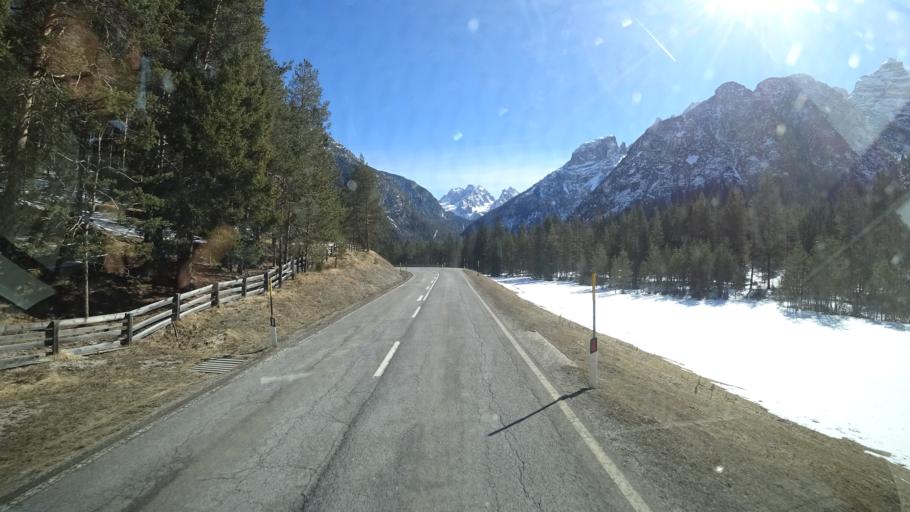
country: IT
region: Trentino-Alto Adige
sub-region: Bolzano
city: Dobbiaco
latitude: 46.6221
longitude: 12.2080
